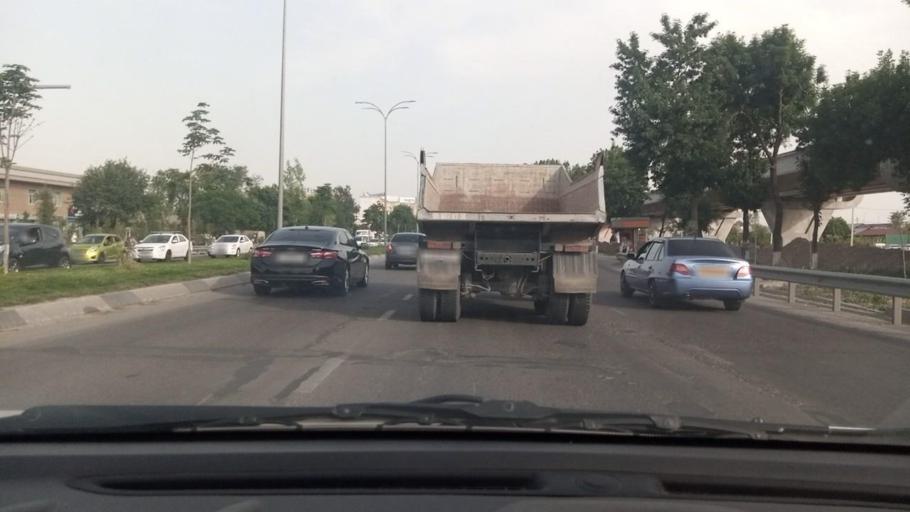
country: UZ
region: Toshkent
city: Salor
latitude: 41.2959
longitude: 69.3529
